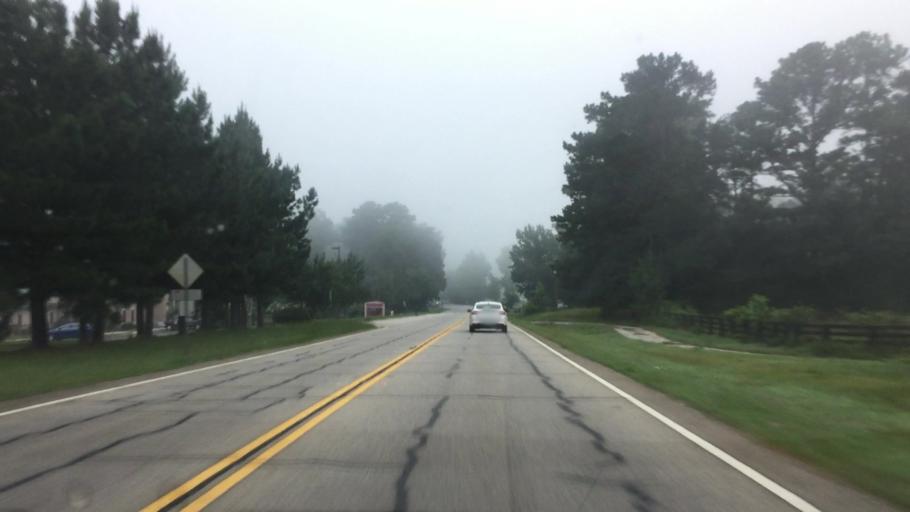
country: US
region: Georgia
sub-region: DeKalb County
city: Pine Mountain
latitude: 33.6047
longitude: -84.1594
